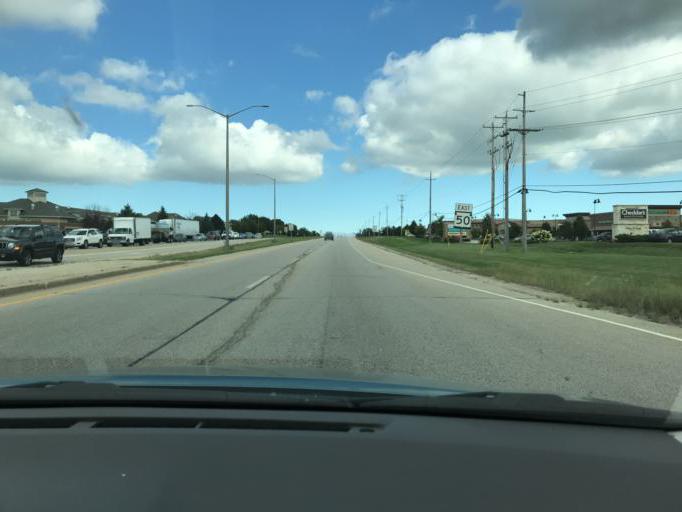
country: US
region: Wisconsin
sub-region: Kenosha County
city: Pleasant Prairie
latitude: 42.5671
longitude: -87.9336
